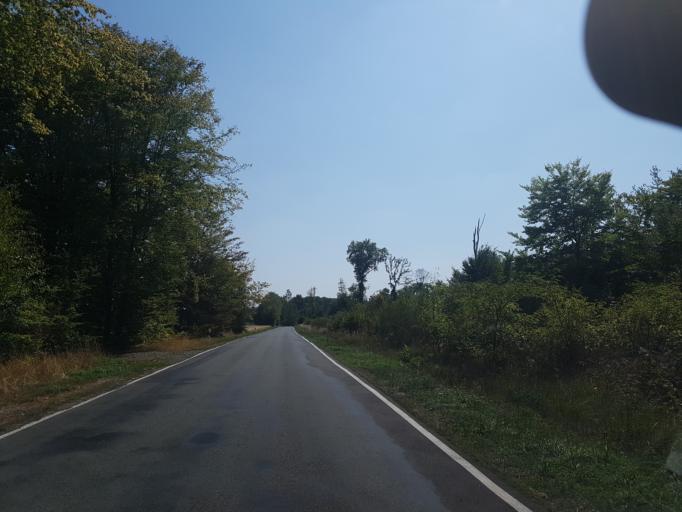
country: DE
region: Brandenburg
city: Wiesenburg
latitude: 52.0310
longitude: 12.3753
